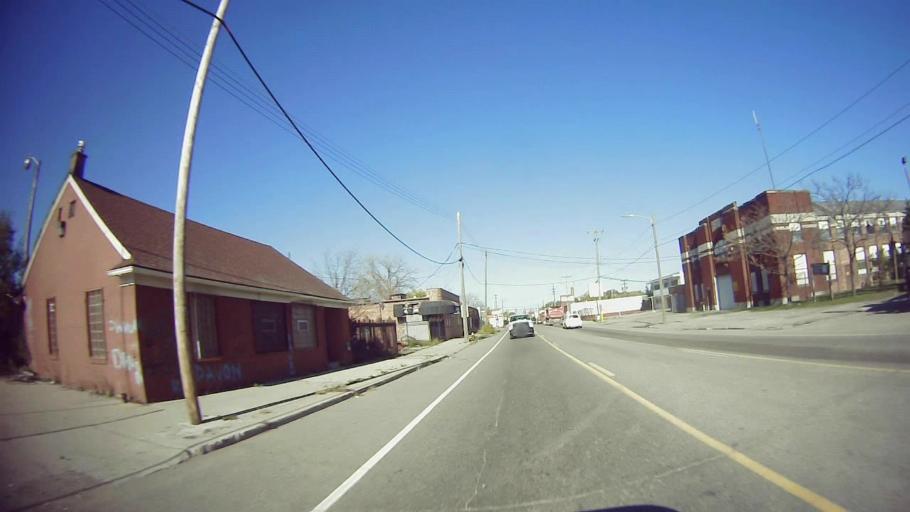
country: US
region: Michigan
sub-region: Wayne County
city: Highland Park
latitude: 42.3939
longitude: -83.1592
